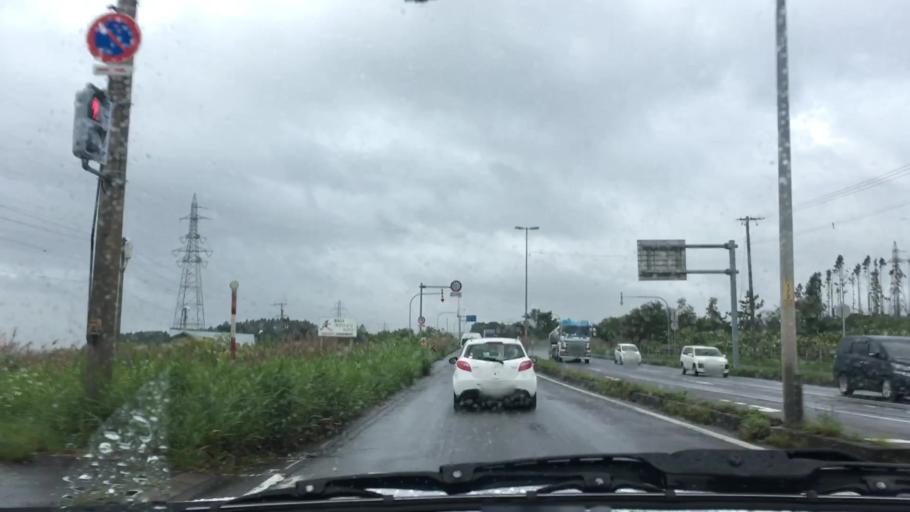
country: JP
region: Hokkaido
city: Nanae
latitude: 42.2458
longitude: 140.2899
